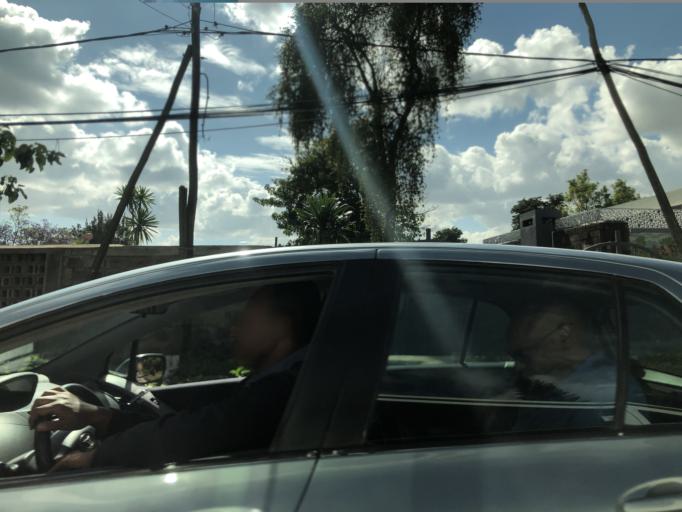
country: ET
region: Adis Abeba
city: Addis Ababa
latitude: 8.9938
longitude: 38.7806
